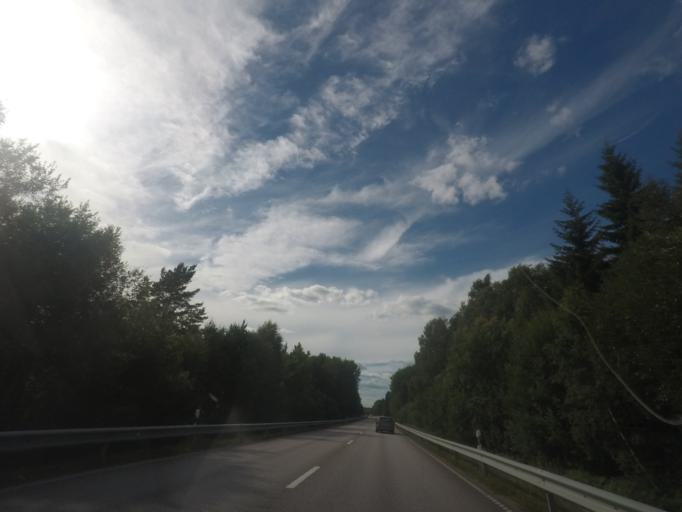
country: SE
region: Stockholm
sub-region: Norrtalje Kommun
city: Skanninge
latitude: 59.8952
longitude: 18.6212
